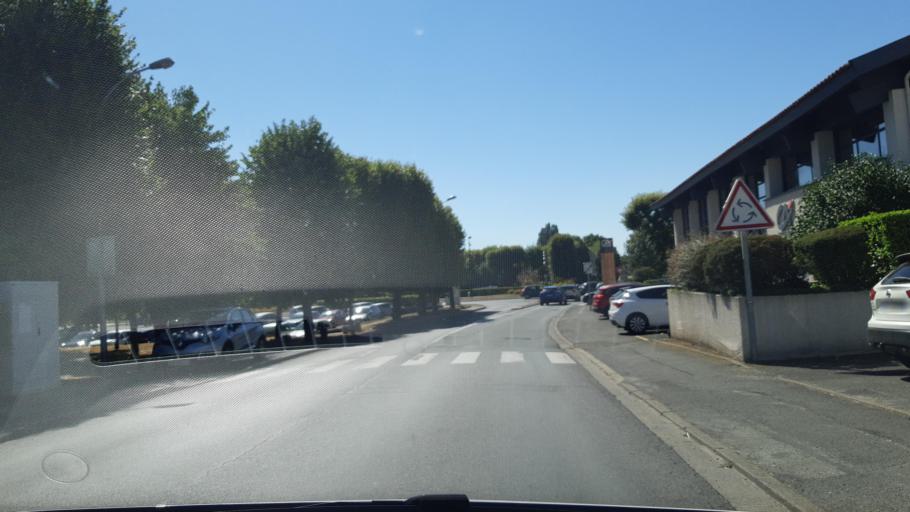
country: FR
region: Poitou-Charentes
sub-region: Departement des Deux-Sevres
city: Exireuil
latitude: 46.4157
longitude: -0.2016
